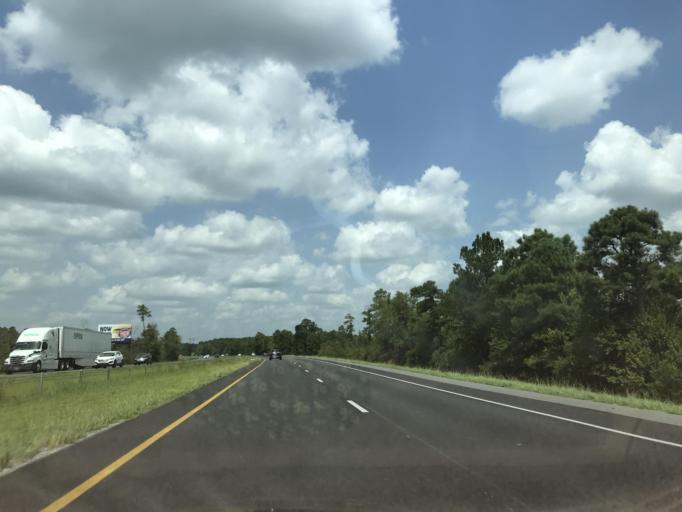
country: US
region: North Carolina
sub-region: Duplin County
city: Wallace
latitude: 34.7856
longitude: -77.9758
